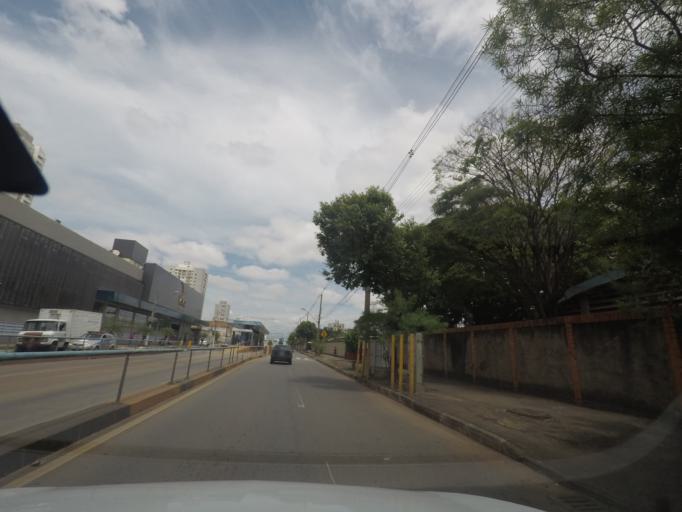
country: BR
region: Goias
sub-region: Goiania
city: Goiania
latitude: -16.6696
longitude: -49.2414
